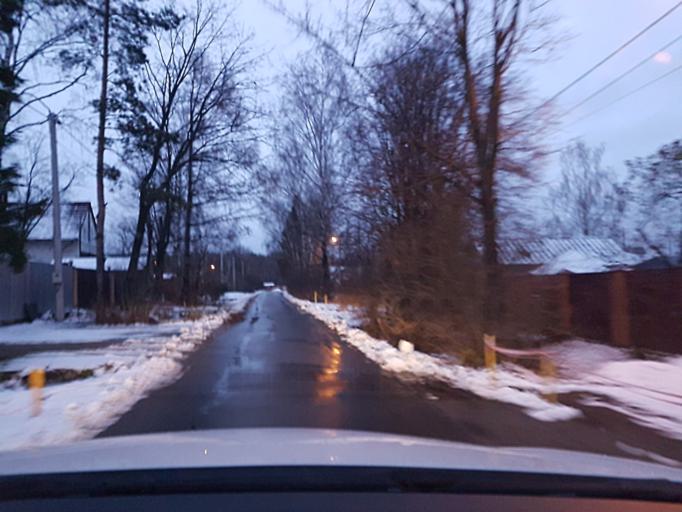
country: RU
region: Moskovskaya
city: Sheremet'yevskiy
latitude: 55.9898
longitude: 37.5243
